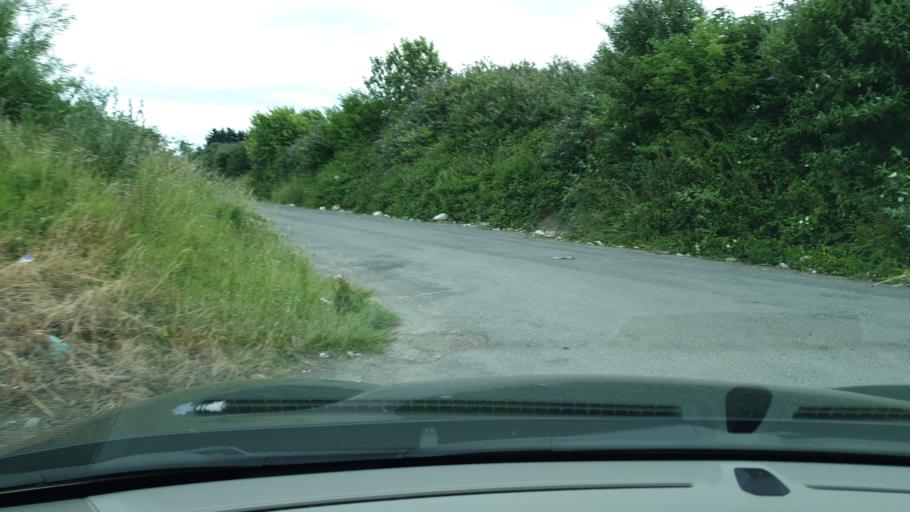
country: IE
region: Leinster
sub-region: Dublin City
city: Finglas
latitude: 53.3862
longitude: -6.3256
